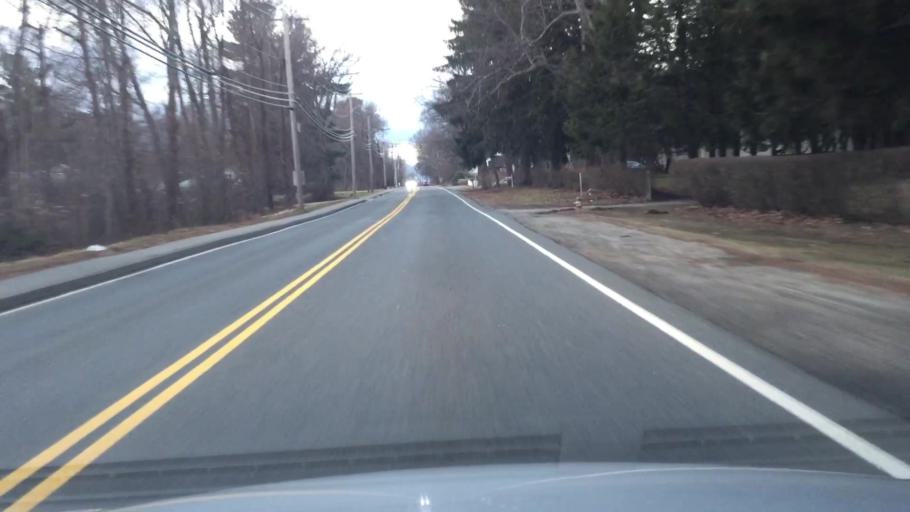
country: US
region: Massachusetts
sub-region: Worcester County
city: West Boylston
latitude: 42.3300
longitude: -71.8152
